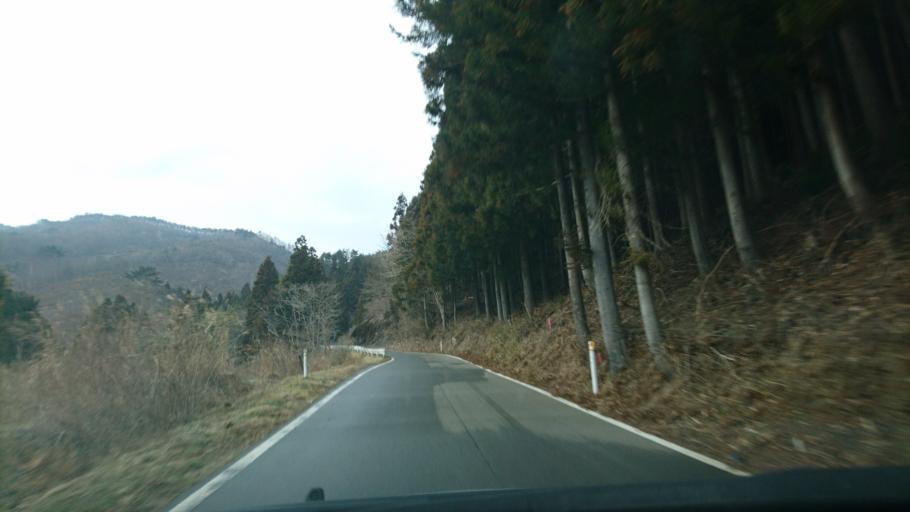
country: JP
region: Iwate
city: Ofunato
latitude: 38.9904
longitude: 141.5514
